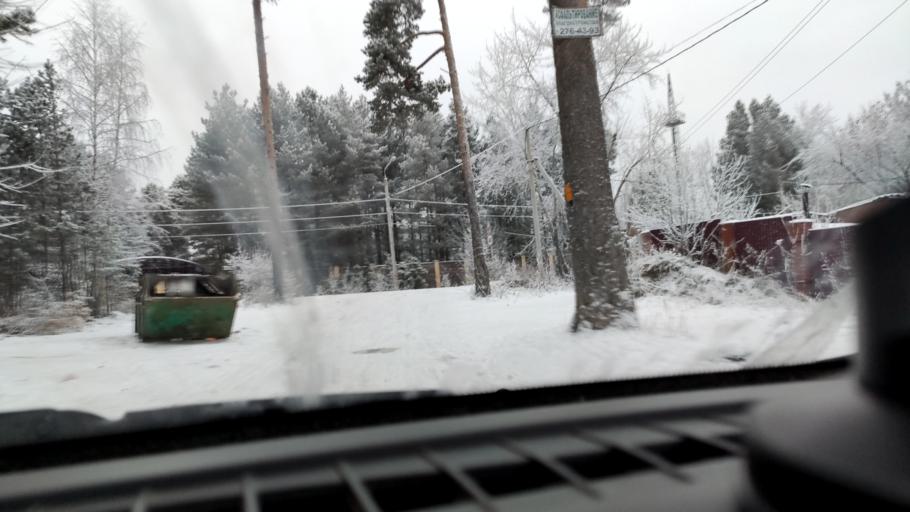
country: RU
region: Perm
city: Perm
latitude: 58.0465
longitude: 56.2819
